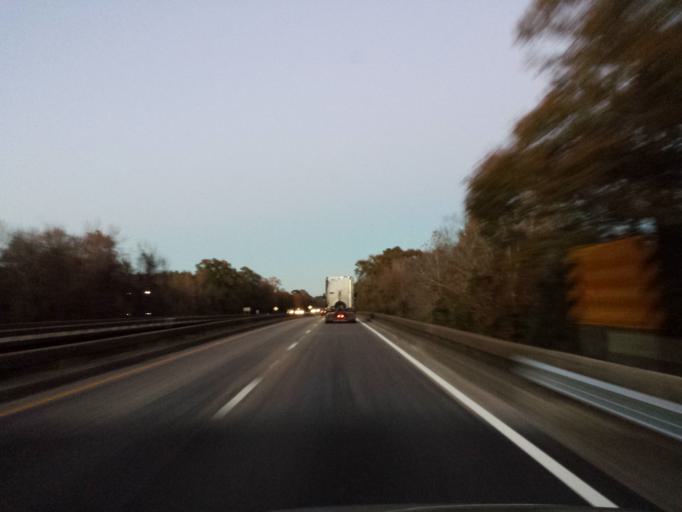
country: US
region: Mississippi
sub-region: Jones County
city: Laurel
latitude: 31.7102
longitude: -89.1124
